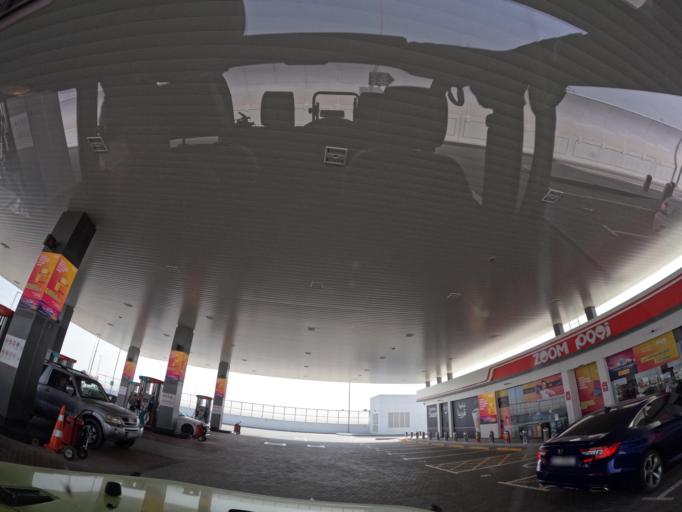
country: AE
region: Dubai
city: Dubai
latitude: 25.1541
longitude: 55.3355
